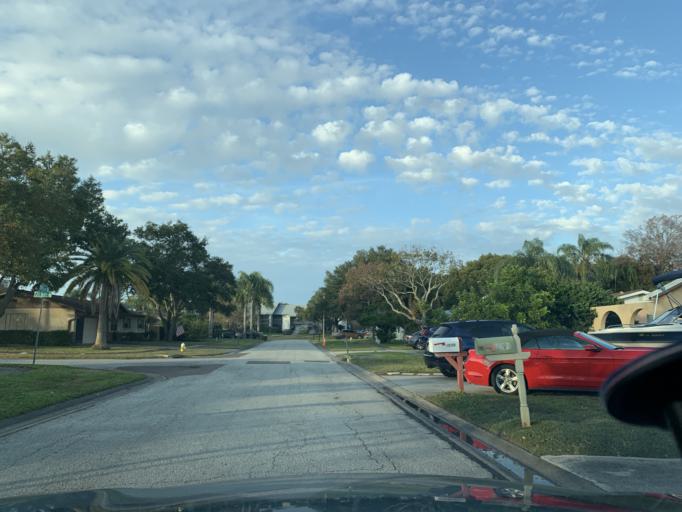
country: US
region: Florida
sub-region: Pinellas County
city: Ridgecrest
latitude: 27.8828
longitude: -82.7936
